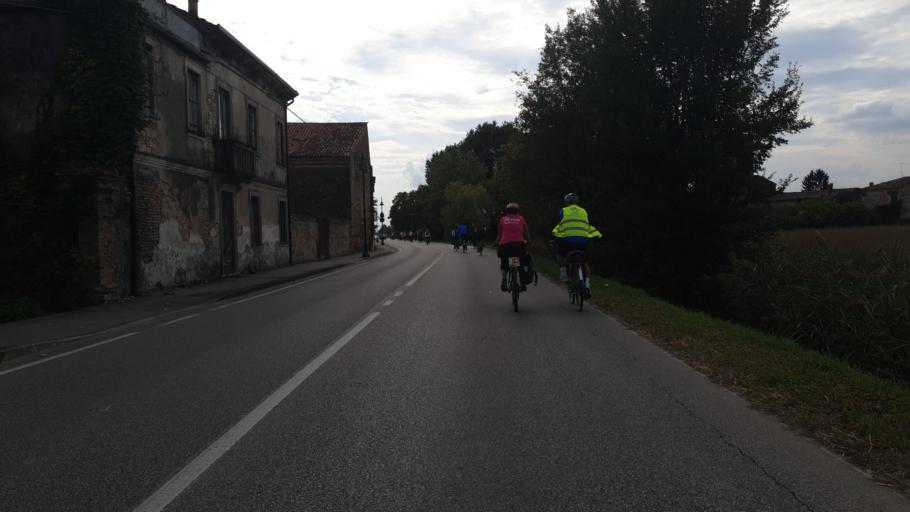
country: IT
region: Veneto
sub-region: Provincia di Vicenza
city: Poiana Maggiore
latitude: 45.2868
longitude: 11.4987
